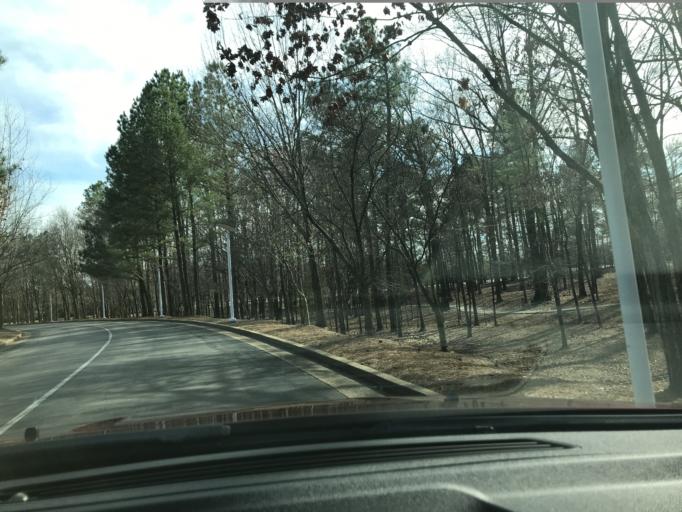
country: US
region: Tennessee
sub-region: Shelby County
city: Germantown
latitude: 35.0498
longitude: -89.7945
